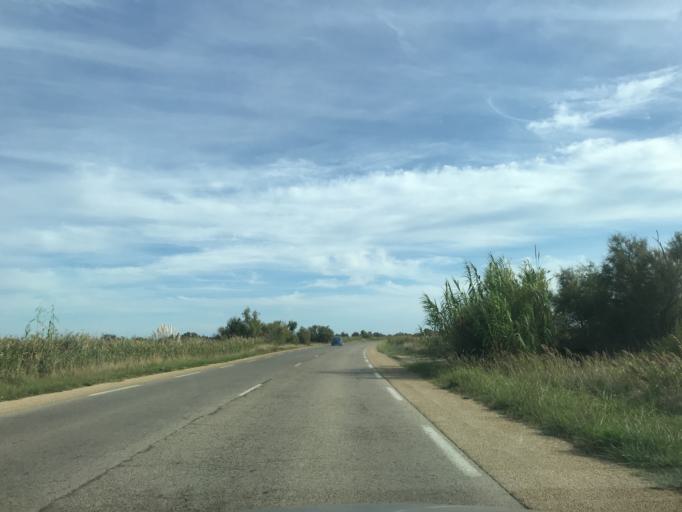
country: FR
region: Provence-Alpes-Cote d'Azur
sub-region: Departement des Bouches-du-Rhone
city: Saintes-Maries-de-la-Mer
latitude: 43.5017
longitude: 4.4020
